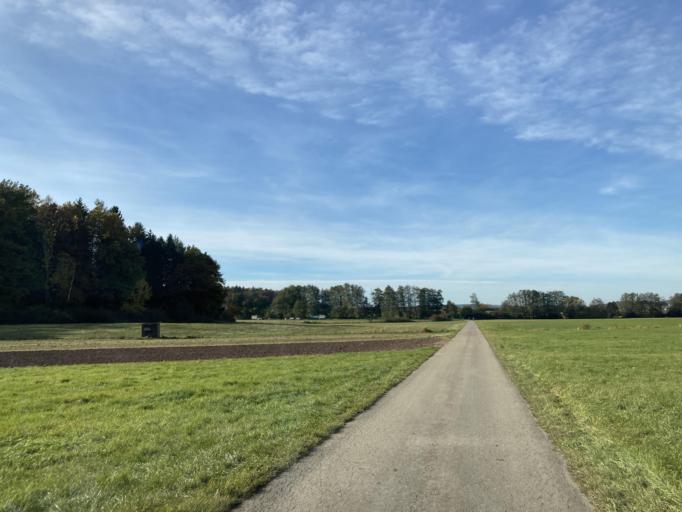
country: DE
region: Baden-Wuerttemberg
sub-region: Tuebingen Region
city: Hirrlingen
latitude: 48.4080
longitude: 8.9324
